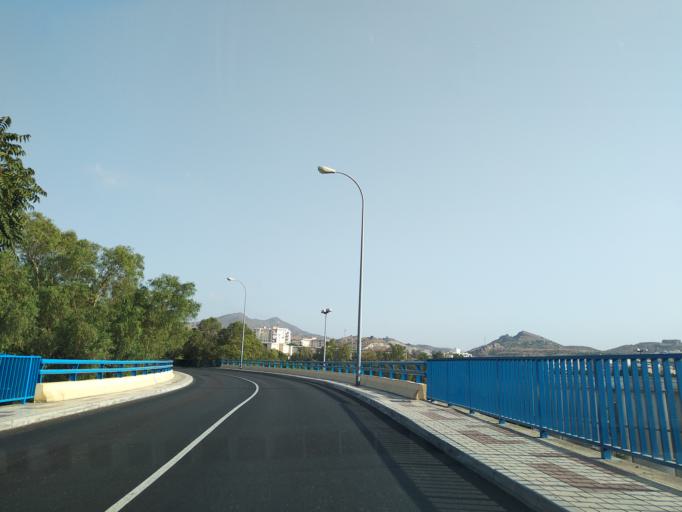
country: ES
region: Andalusia
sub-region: Provincia de Malaga
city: Malaga
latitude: 36.7267
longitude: -4.4489
